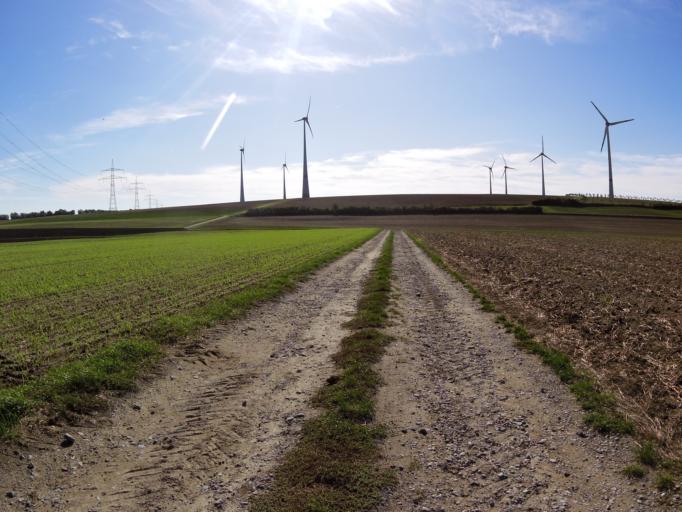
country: DE
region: Bavaria
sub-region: Regierungsbezirk Unterfranken
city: Theilheim
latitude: 49.7267
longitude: 10.0480
